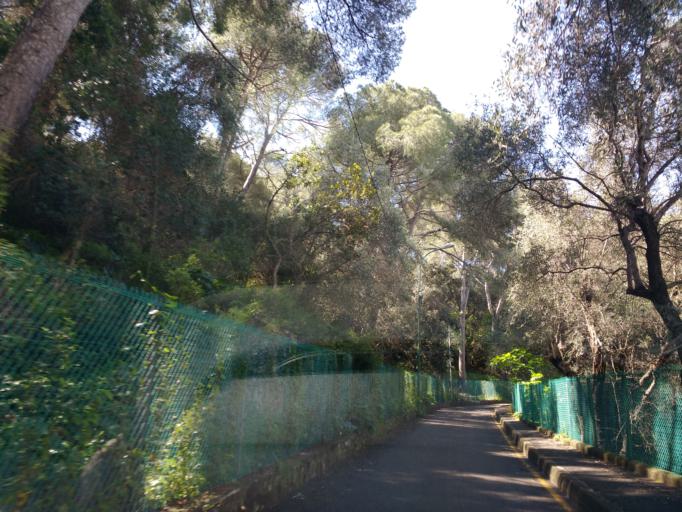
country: FR
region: Provence-Alpes-Cote d'Azur
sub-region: Departement des Alpes-Maritimes
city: Saint-Jean-Cap-Ferrat
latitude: 43.6930
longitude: 7.3253
